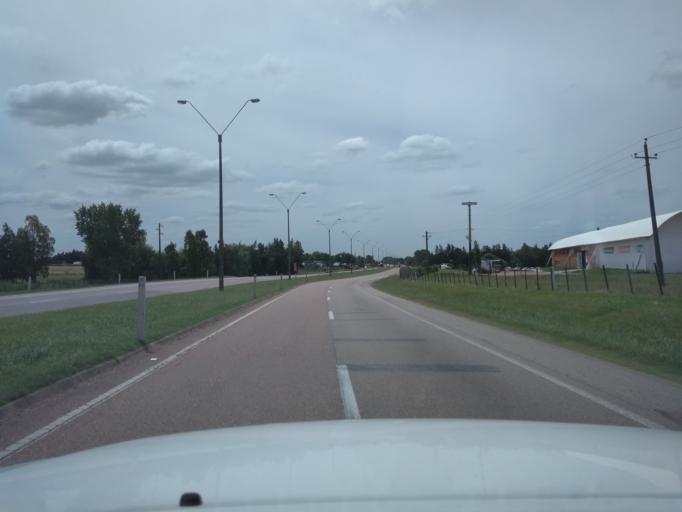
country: UY
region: Canelones
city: Joanico
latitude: -34.5997
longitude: -56.2616
